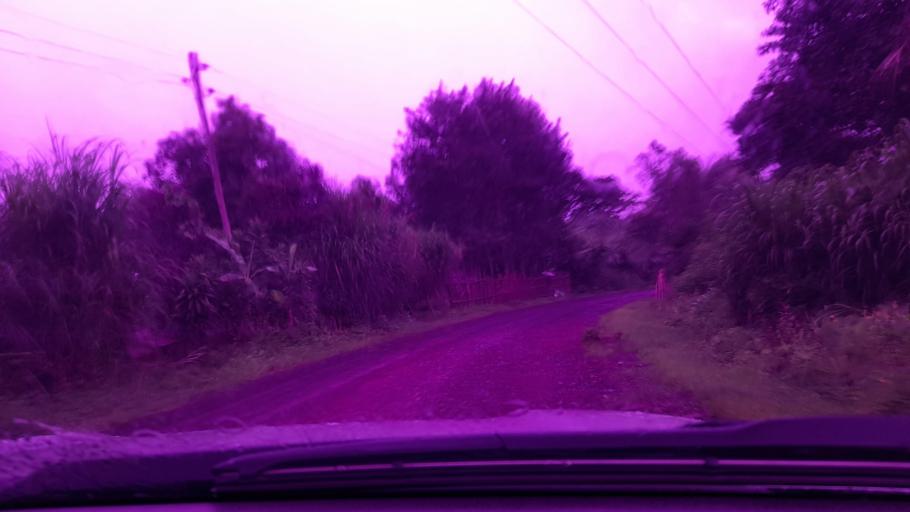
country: ET
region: Oromiya
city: Metu
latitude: 8.4582
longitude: 35.6372
